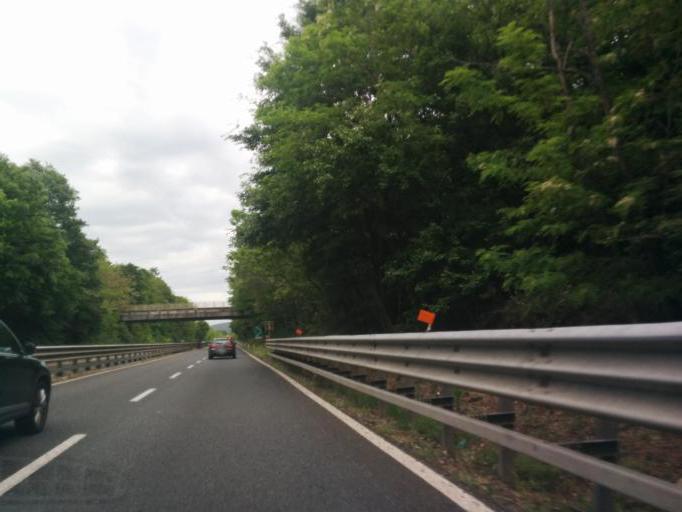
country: IT
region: Tuscany
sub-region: Provincia di Siena
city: Staggia
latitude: 43.4063
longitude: 11.1803
